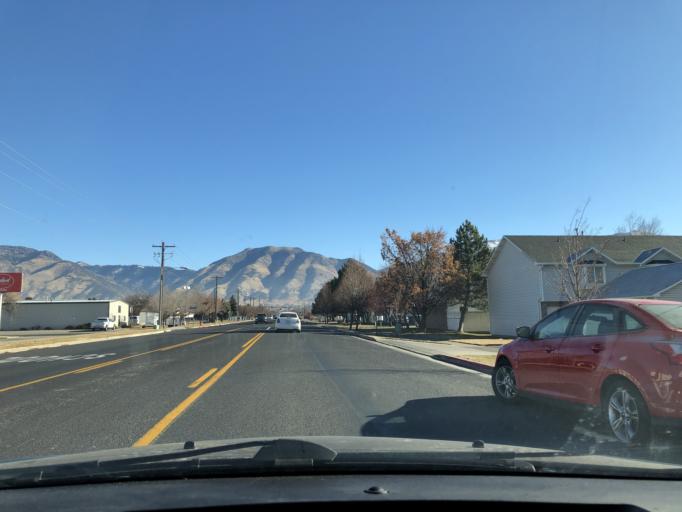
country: US
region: Utah
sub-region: Cache County
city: Logan
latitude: 41.7578
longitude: -111.8428
